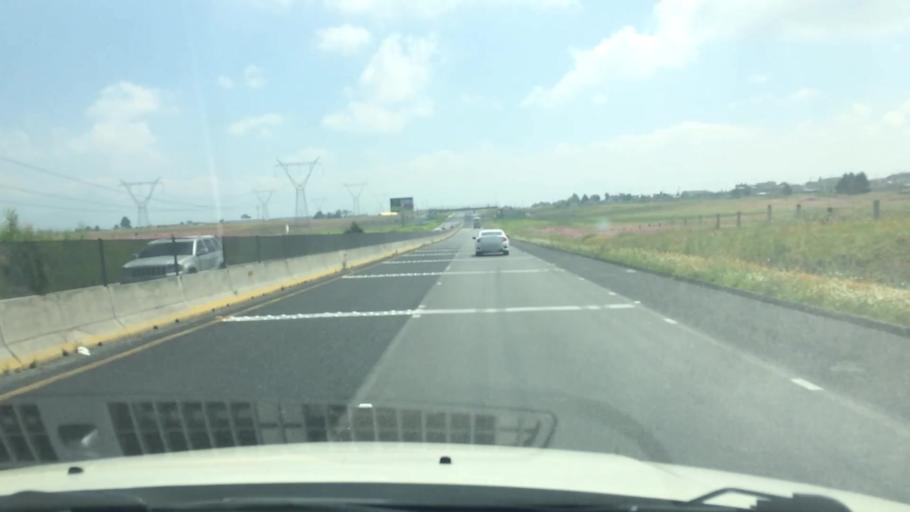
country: MX
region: Mexico
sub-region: Toluca
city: Galaxias Toluca
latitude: 19.3941
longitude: -99.6506
